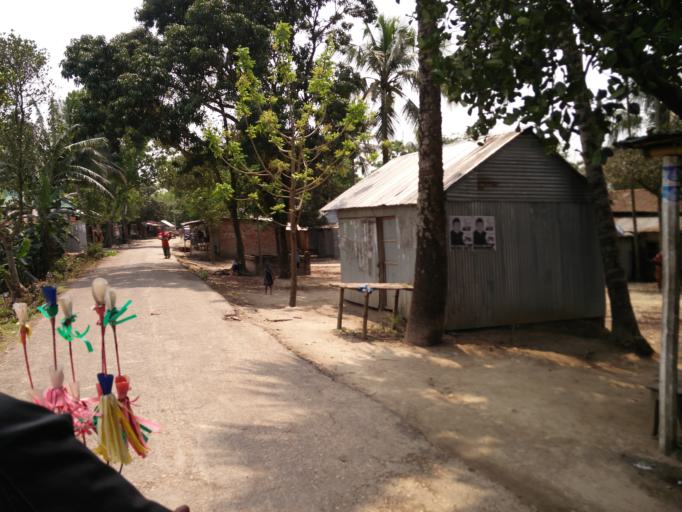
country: BD
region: Dhaka
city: Sherpur
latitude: 24.9362
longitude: 90.1589
